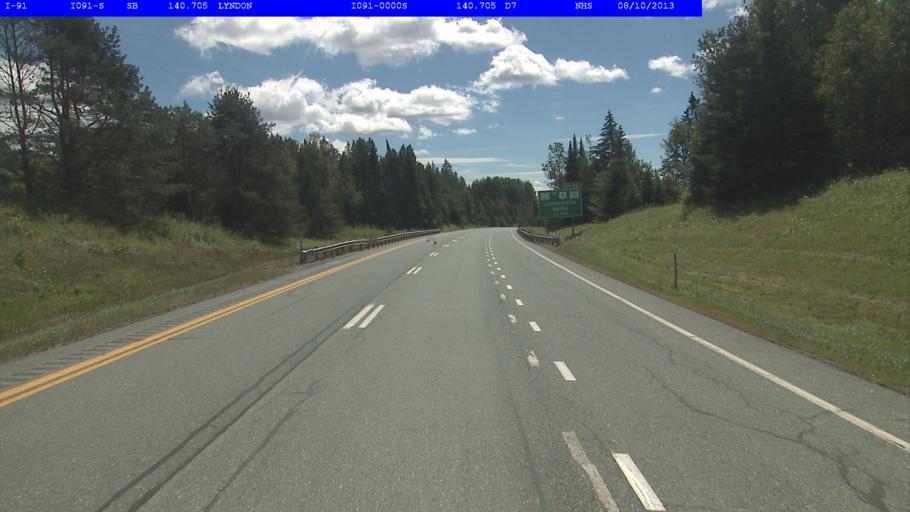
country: US
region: Vermont
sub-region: Caledonia County
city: Lyndonville
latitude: 44.5641
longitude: -72.0317
